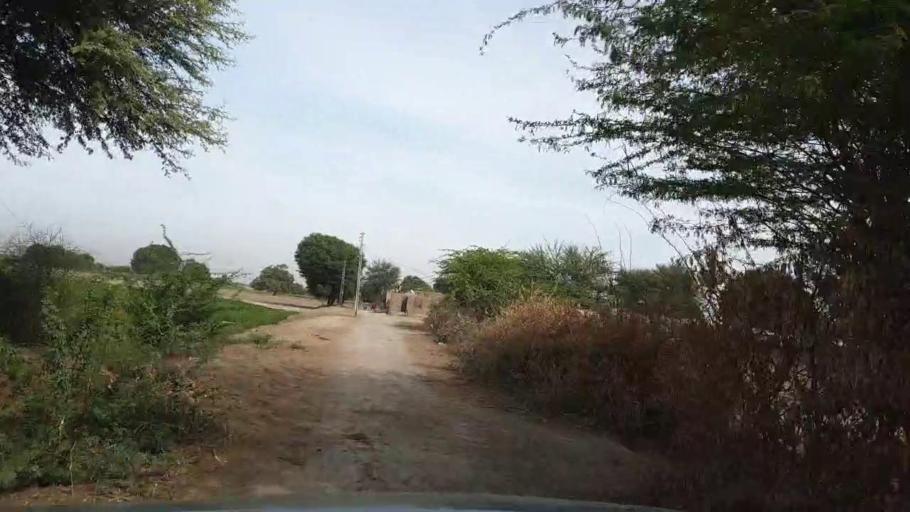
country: PK
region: Sindh
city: Kunri
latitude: 25.1660
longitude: 69.6224
